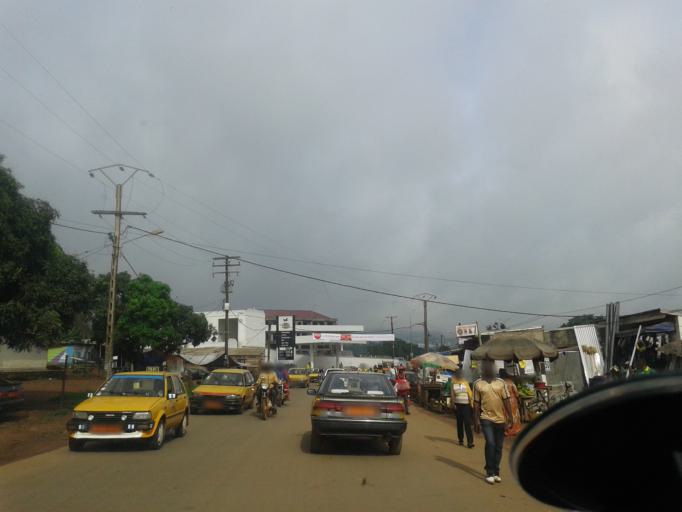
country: CM
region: Centre
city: Yaounde
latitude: 3.9168
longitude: 11.5214
